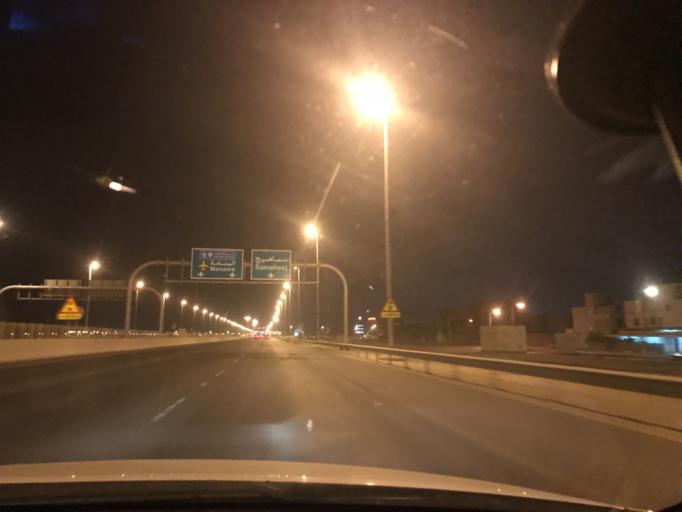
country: BH
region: Muharraq
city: Al Muharraq
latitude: 26.2862
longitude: 50.6401
